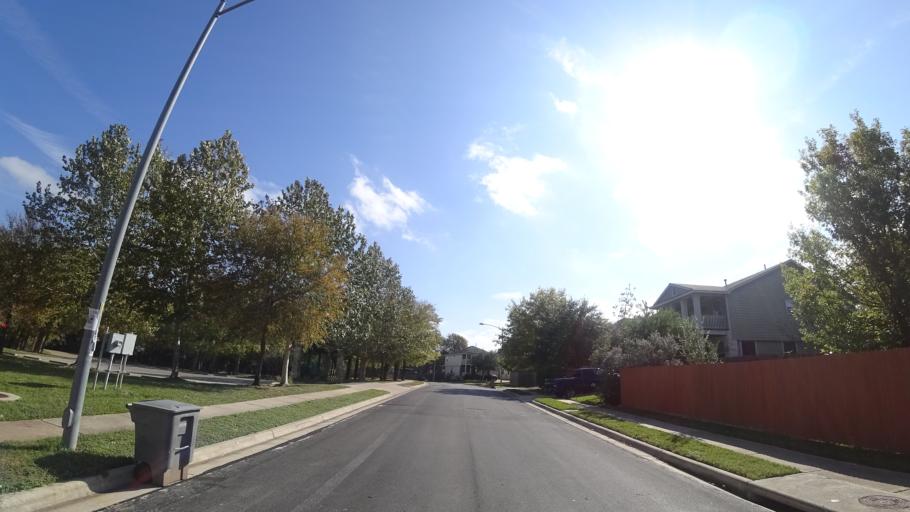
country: US
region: Texas
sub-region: Travis County
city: Shady Hollow
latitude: 30.1916
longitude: -97.8196
